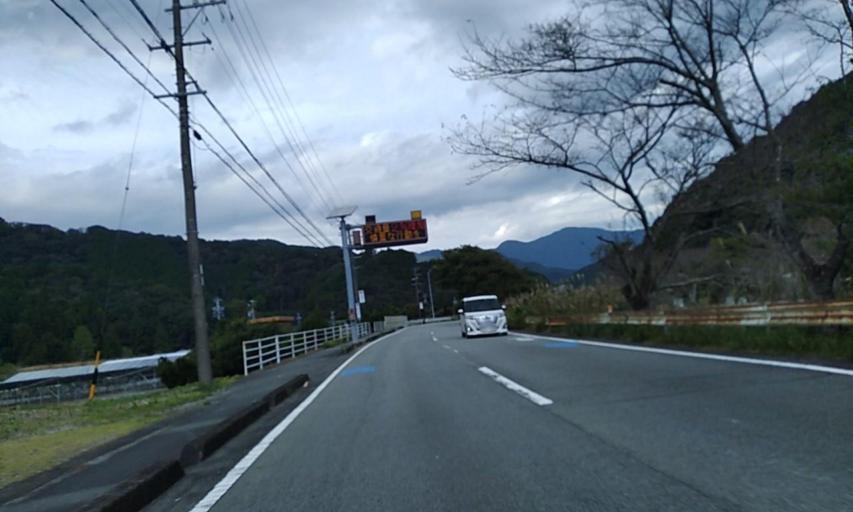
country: JP
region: Mie
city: Ise
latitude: 34.2821
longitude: 136.5111
